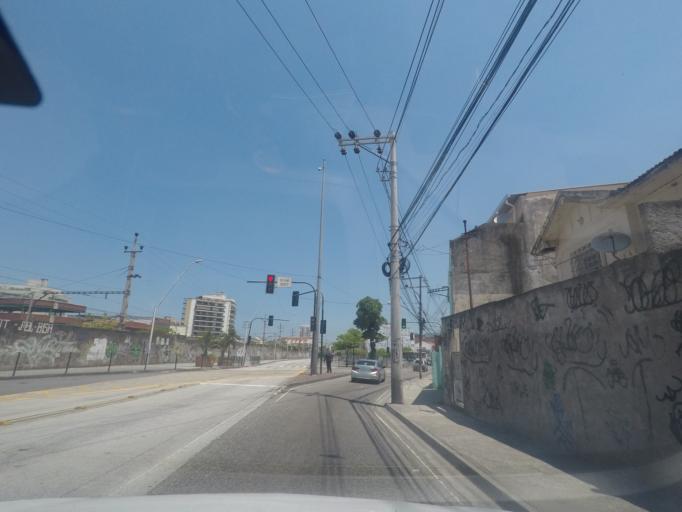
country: BR
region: Rio de Janeiro
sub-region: Duque De Caxias
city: Duque de Caxias
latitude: -22.8452
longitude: -43.2682
